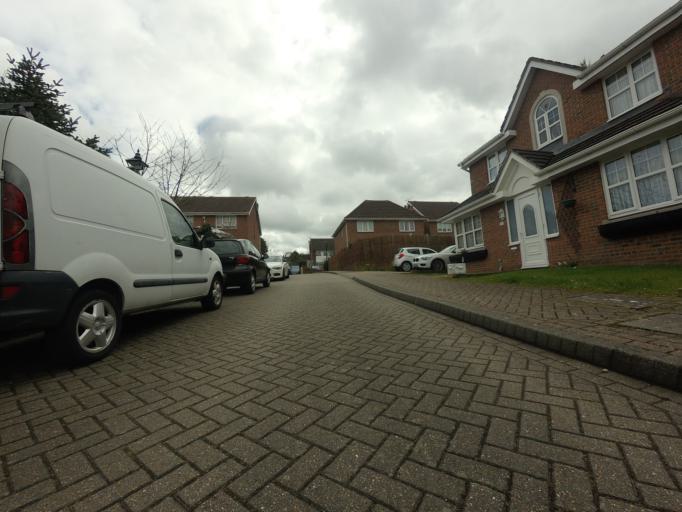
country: GB
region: England
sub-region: Kent
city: Swanley
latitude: 51.3947
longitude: 0.1853
